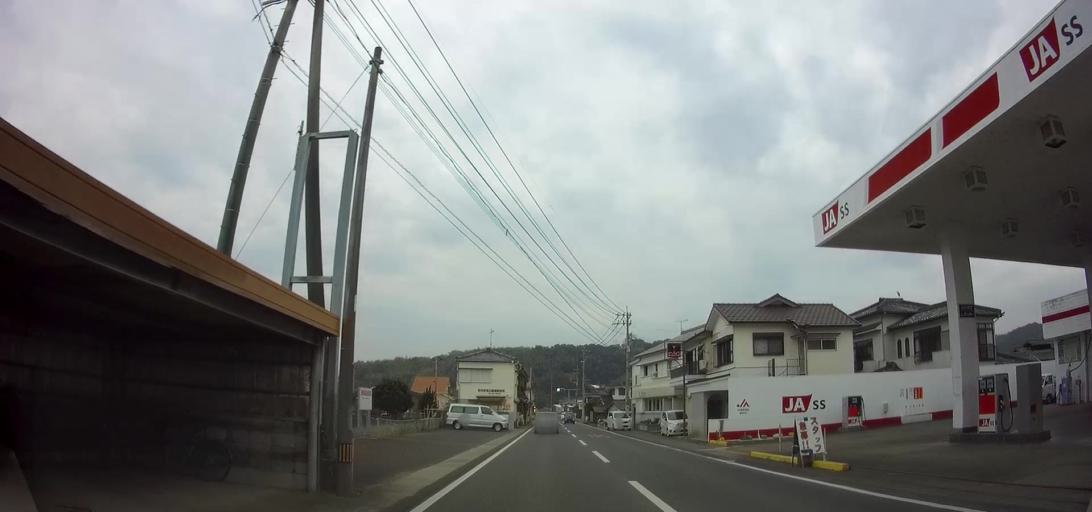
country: JP
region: Nagasaki
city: Shimabara
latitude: 32.6543
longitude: 130.2726
